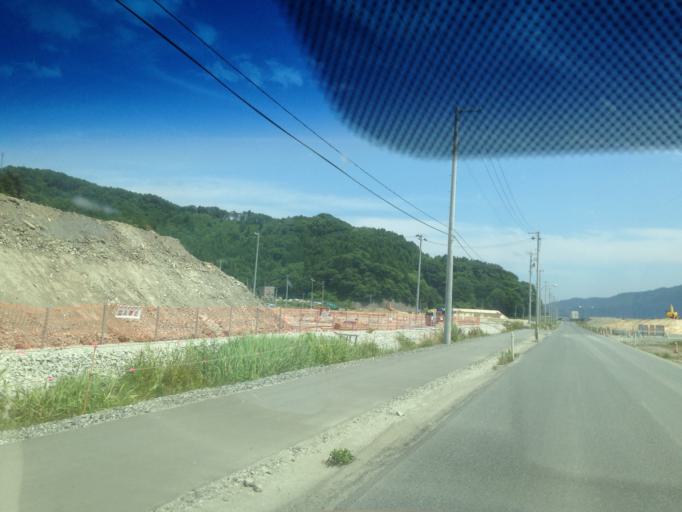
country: JP
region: Iwate
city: Otsuchi
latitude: 39.3589
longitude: 141.9147
